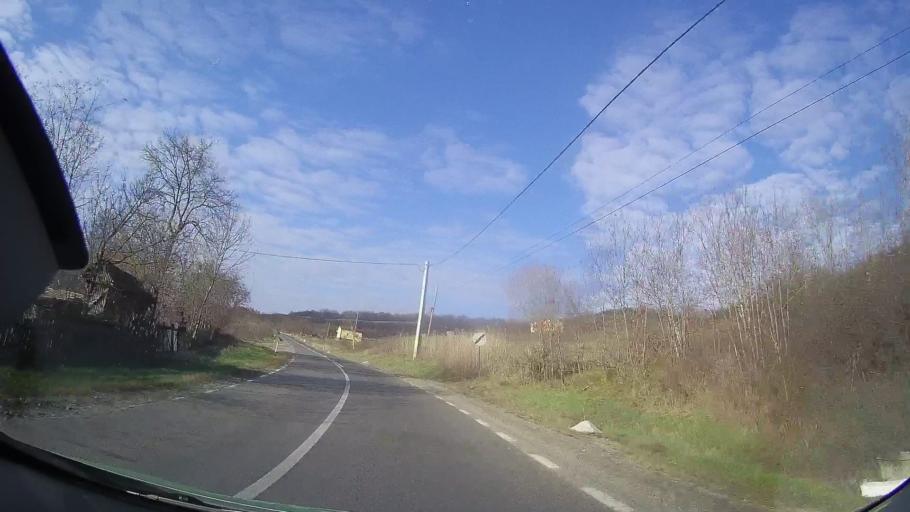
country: RO
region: Cluj
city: Jucu Herghelia
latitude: 46.8080
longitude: 23.8402
